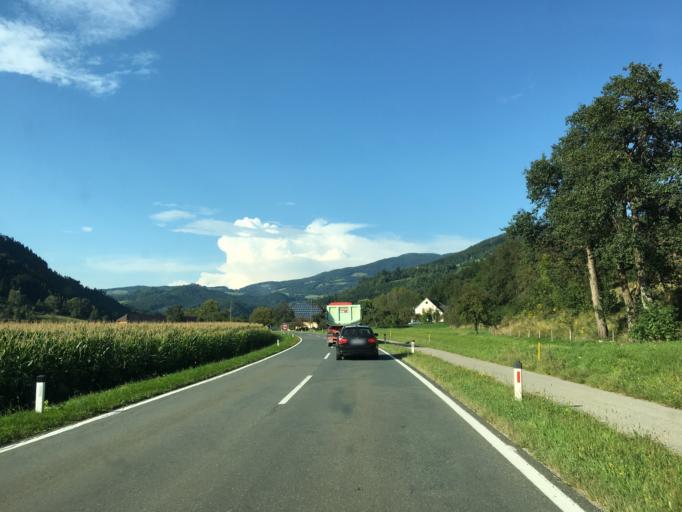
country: AT
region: Carinthia
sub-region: Politischer Bezirk Sankt Veit an der Glan
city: Eberstein
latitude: 46.7888
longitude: 14.5528
